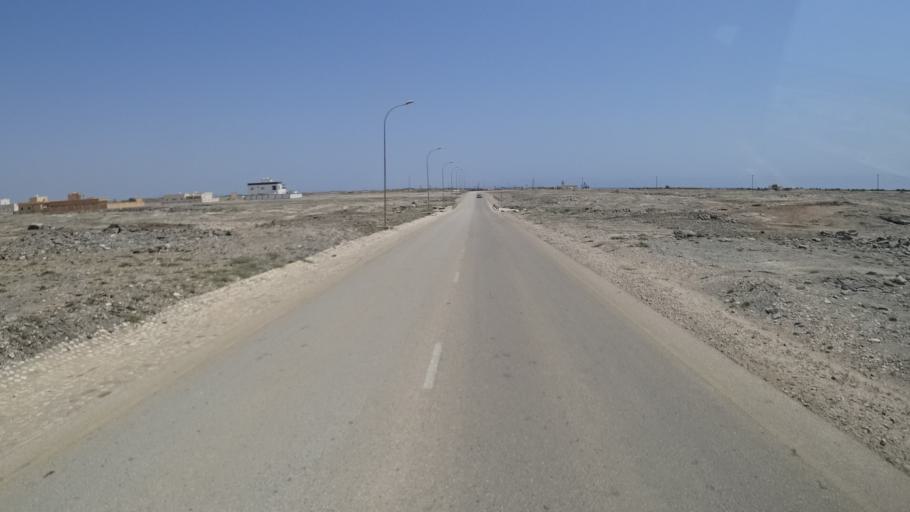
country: OM
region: Zufar
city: Salalah
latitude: 16.9672
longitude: 54.7341
